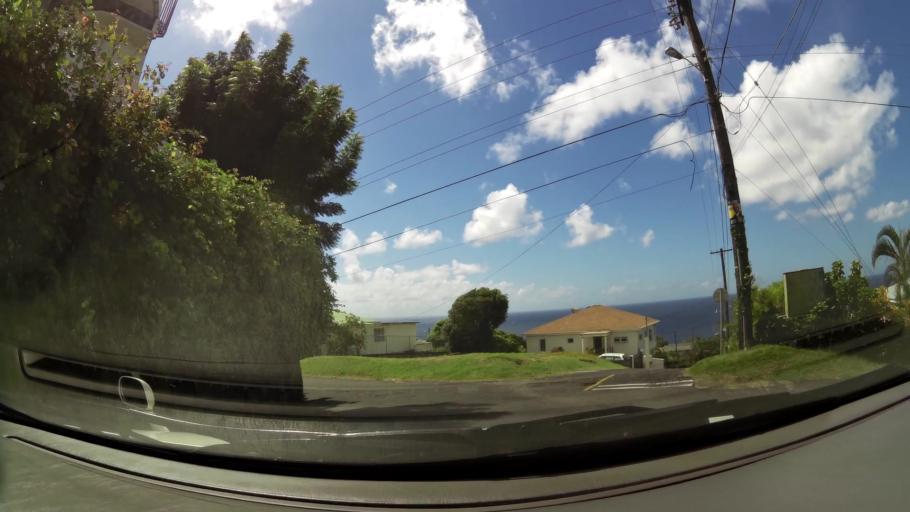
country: VC
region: Saint George
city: Kingstown
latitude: 13.1434
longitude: -61.2233
